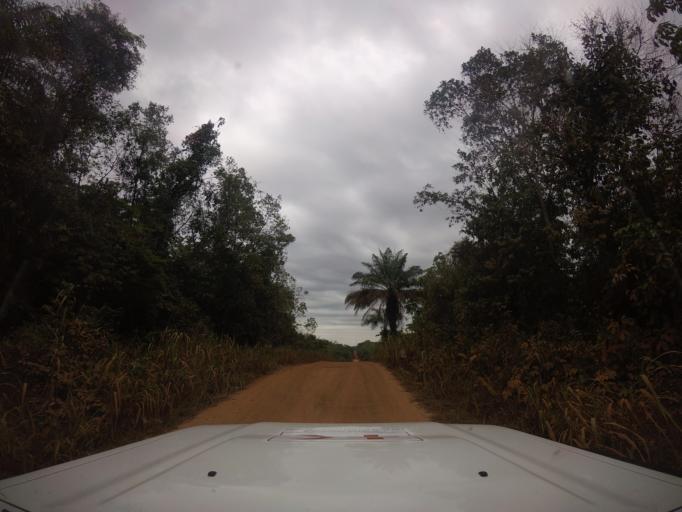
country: LR
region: Grand Cape Mount
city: Robertsport
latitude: 6.9551
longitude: -11.3211
